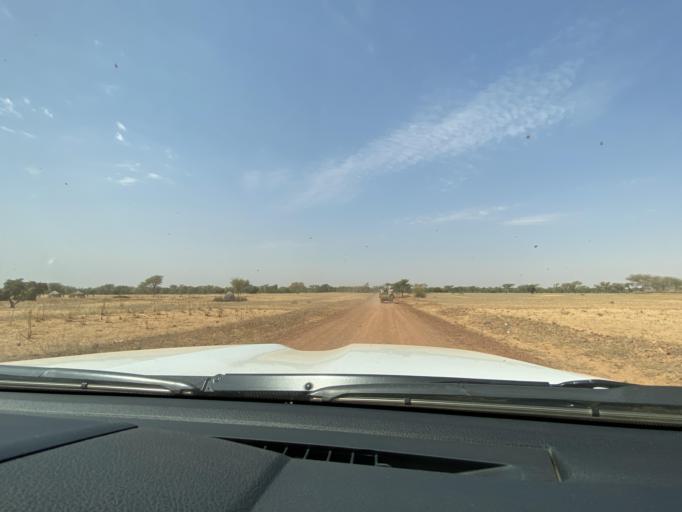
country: NE
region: Dosso
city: Birnin Gaoure
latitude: 13.2445
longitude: 2.8626
